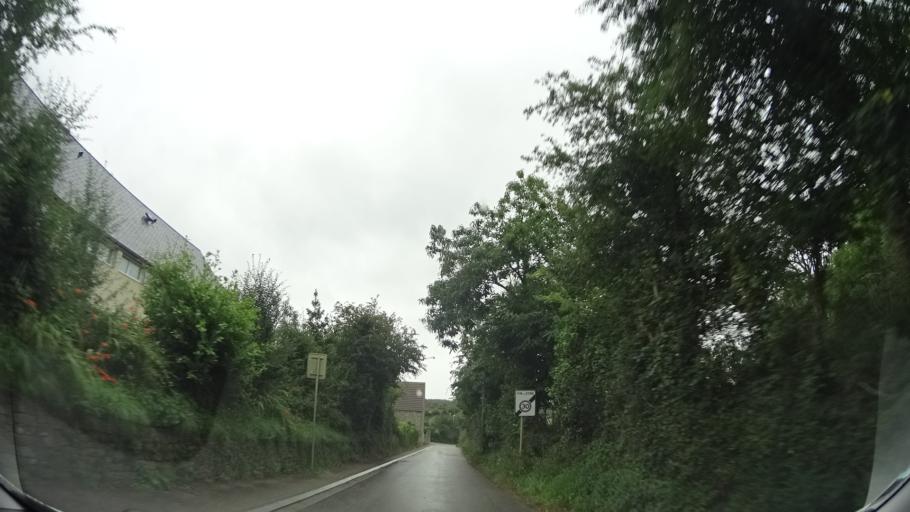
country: FR
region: Lower Normandy
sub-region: Departement de la Manche
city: Beaumont-Hague
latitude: 49.6120
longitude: -1.8230
